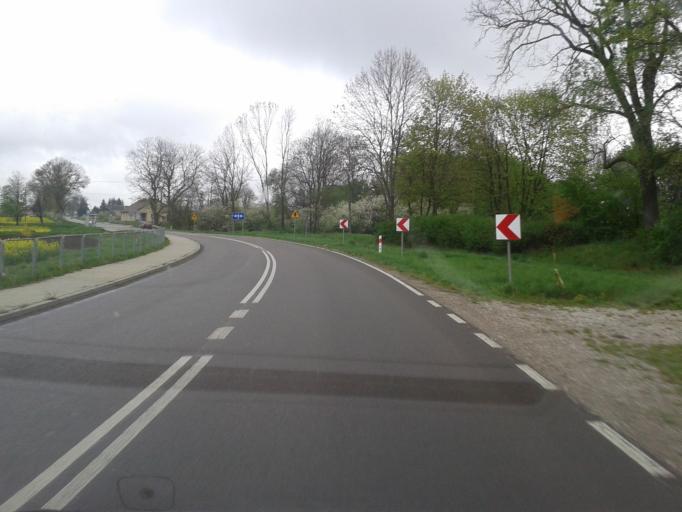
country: PL
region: Lublin Voivodeship
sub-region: Powiat hrubieszowski
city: Dolhobyczow
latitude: 50.5881
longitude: 23.9982
